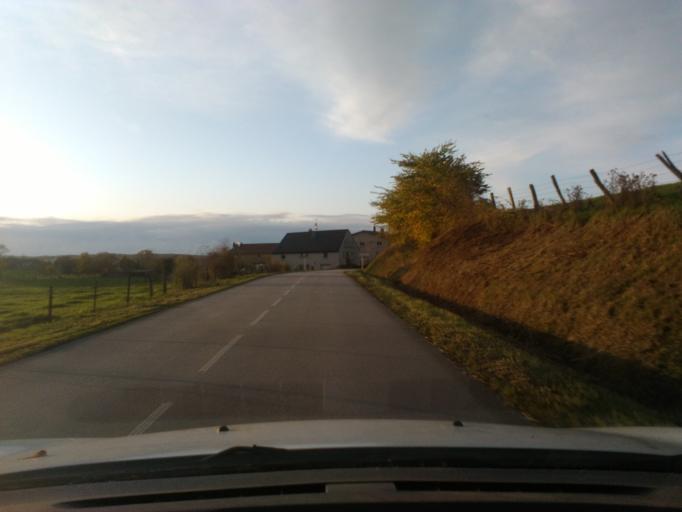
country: FR
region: Lorraine
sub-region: Departement des Vosges
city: Mirecourt
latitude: 48.2599
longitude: 6.1781
